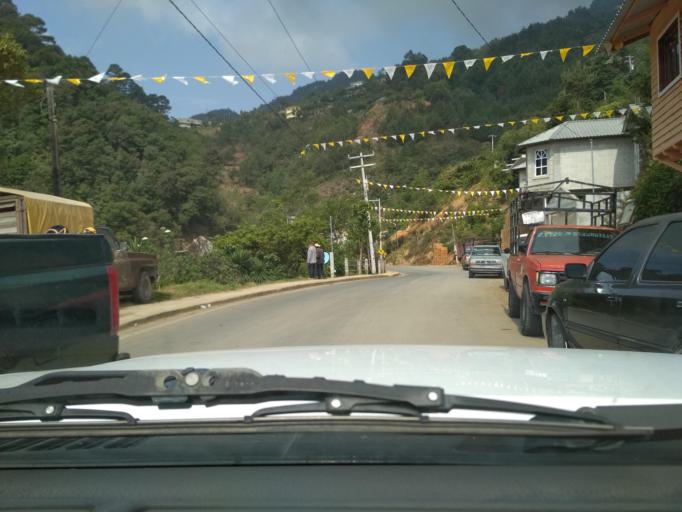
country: MX
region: Veracruz
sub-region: Soledad Atzompa
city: Tlatilpa
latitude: 18.7551
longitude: -97.1535
